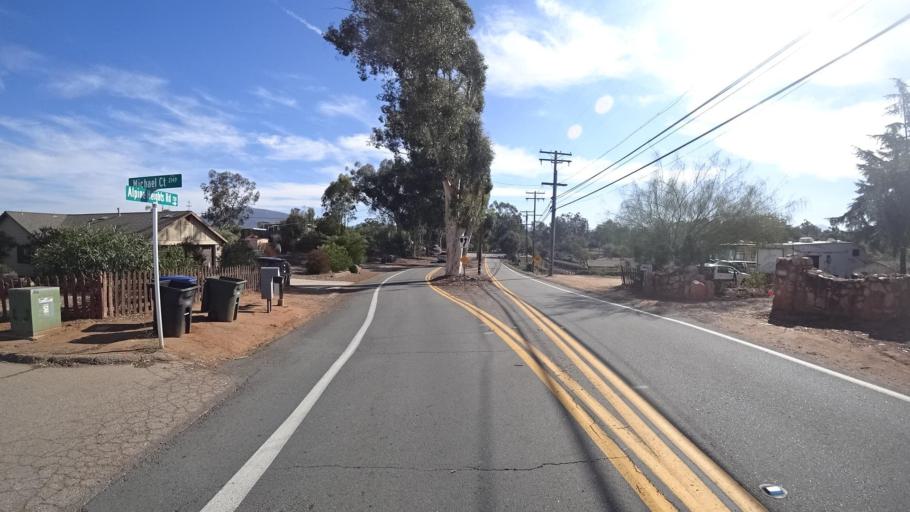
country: US
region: California
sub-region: San Diego County
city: Harbison Canyon
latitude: 32.8190
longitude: -116.7992
